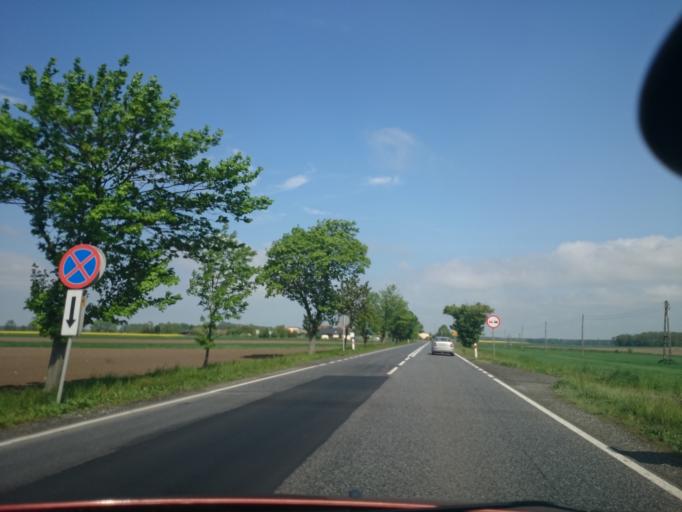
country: PL
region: Opole Voivodeship
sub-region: Powiat opolski
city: Dabrowa
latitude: 50.7167
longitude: 17.7723
